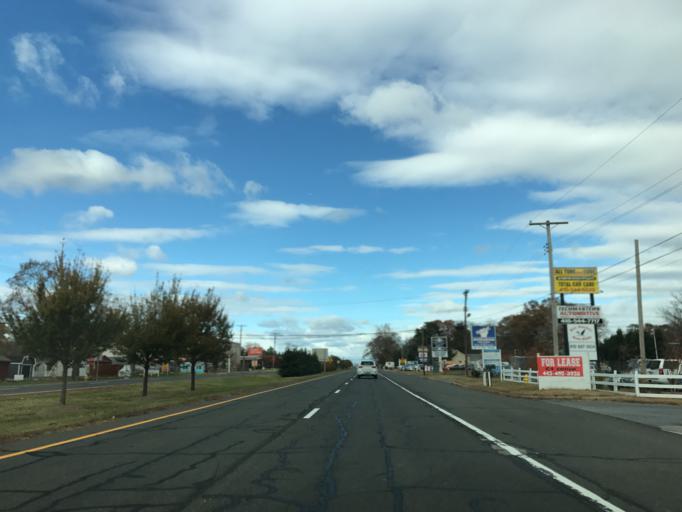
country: US
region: Maryland
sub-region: Anne Arundel County
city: Pasadena
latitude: 39.1194
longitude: -76.5835
